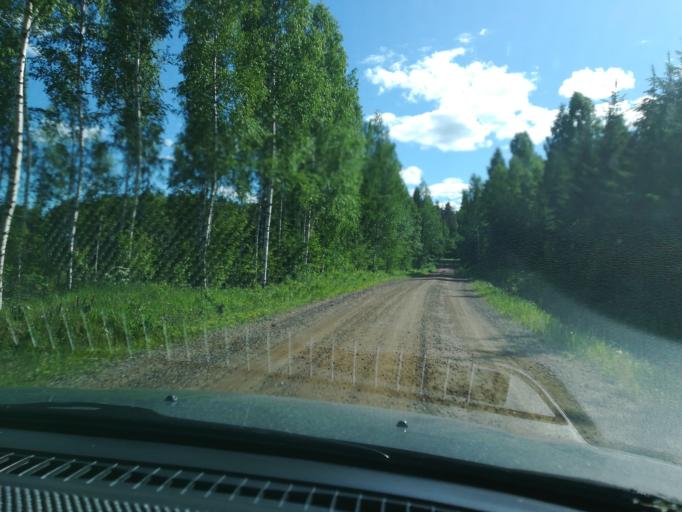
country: FI
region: Southern Savonia
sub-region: Mikkeli
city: Puumala
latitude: 61.6644
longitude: 28.1439
